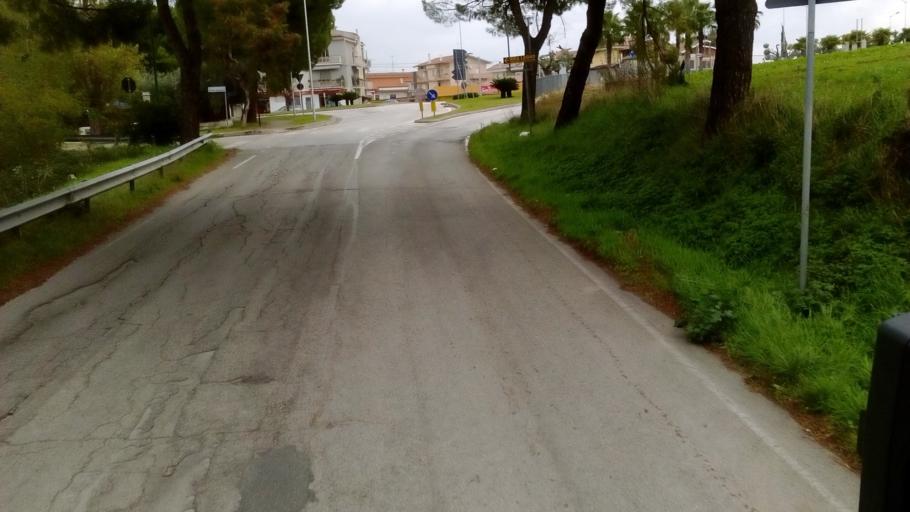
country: IT
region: Abruzzo
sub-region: Provincia di Chieti
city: San Salvo
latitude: 42.0556
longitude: 14.7329
